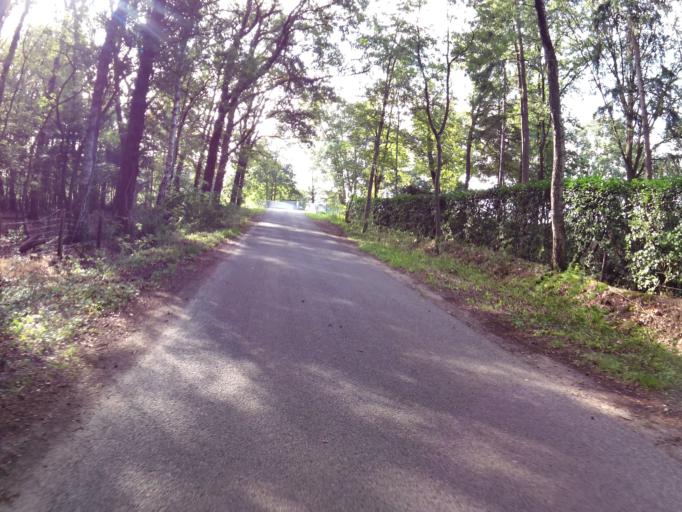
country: NL
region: Overijssel
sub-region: Gemeente Haaksbergen
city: Haaksbergen
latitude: 52.1517
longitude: 6.8180
